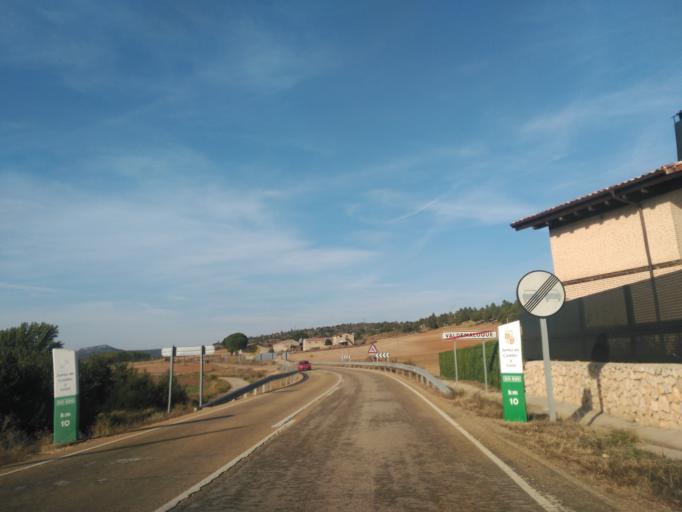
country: ES
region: Castille and Leon
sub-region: Provincia de Soria
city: Valdemaluque
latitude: 41.6747
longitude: -3.0460
